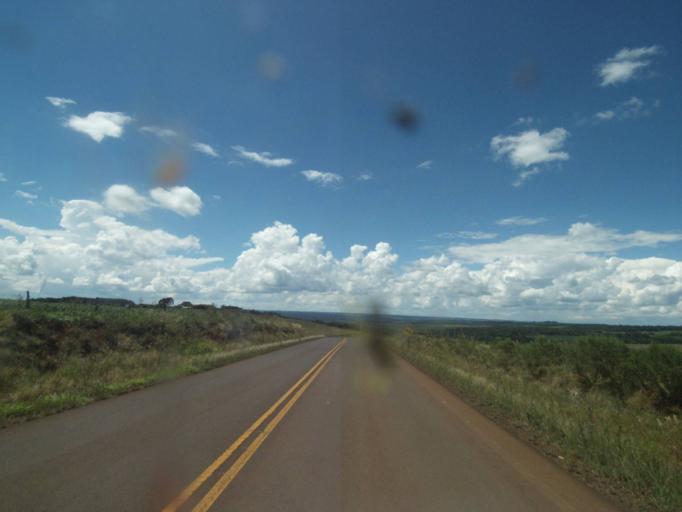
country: BR
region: Parana
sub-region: Pinhao
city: Pinhao
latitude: -25.7983
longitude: -52.0748
